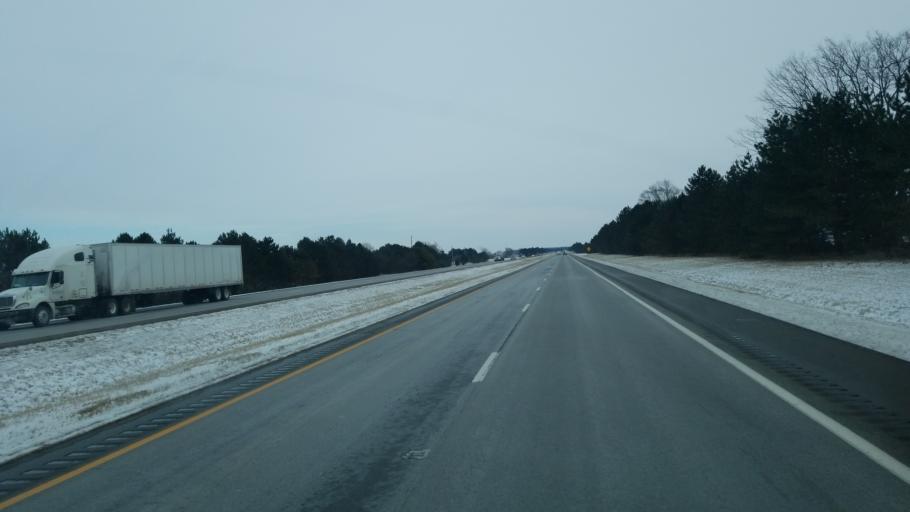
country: US
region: Ohio
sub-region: Wyandot County
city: Carey
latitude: 40.9587
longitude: -83.4537
